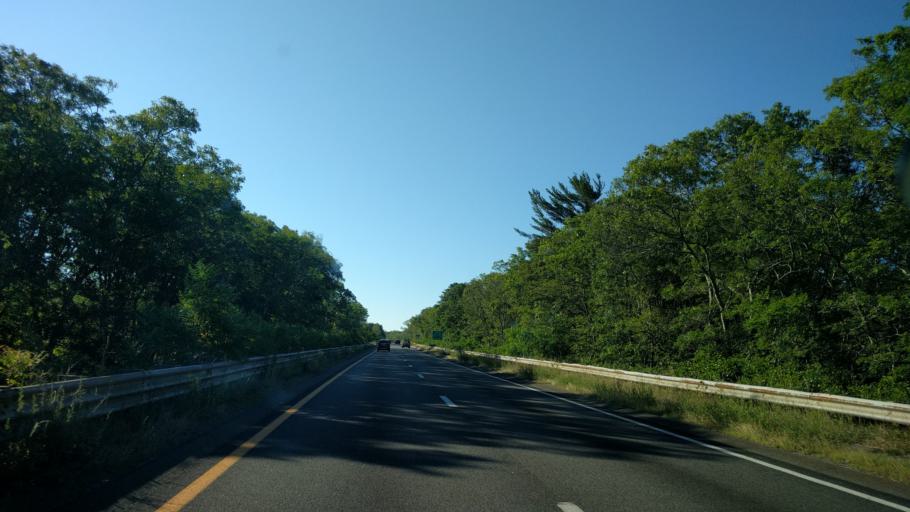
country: US
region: Massachusetts
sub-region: Barnstable County
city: West Barnstable
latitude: 41.7141
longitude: -70.4164
